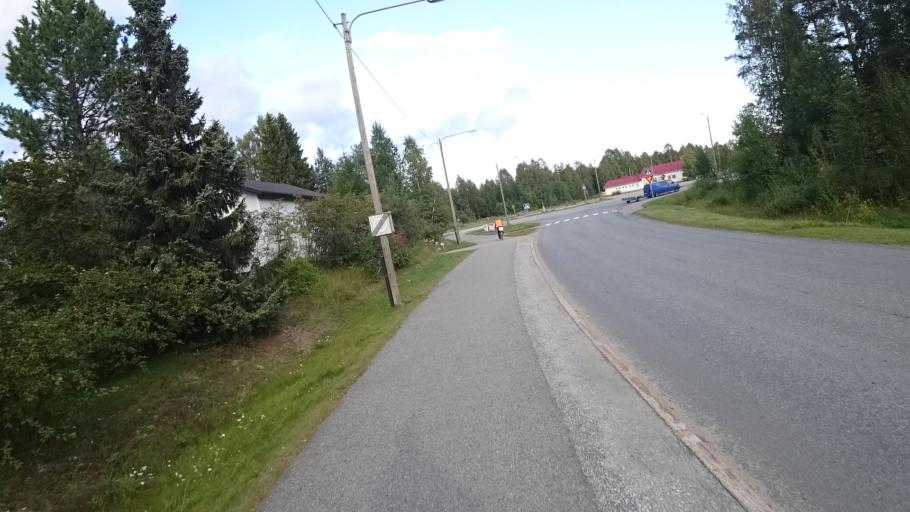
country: FI
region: North Karelia
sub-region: Joensuu
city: Ilomantsi
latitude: 62.6722
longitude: 30.9452
